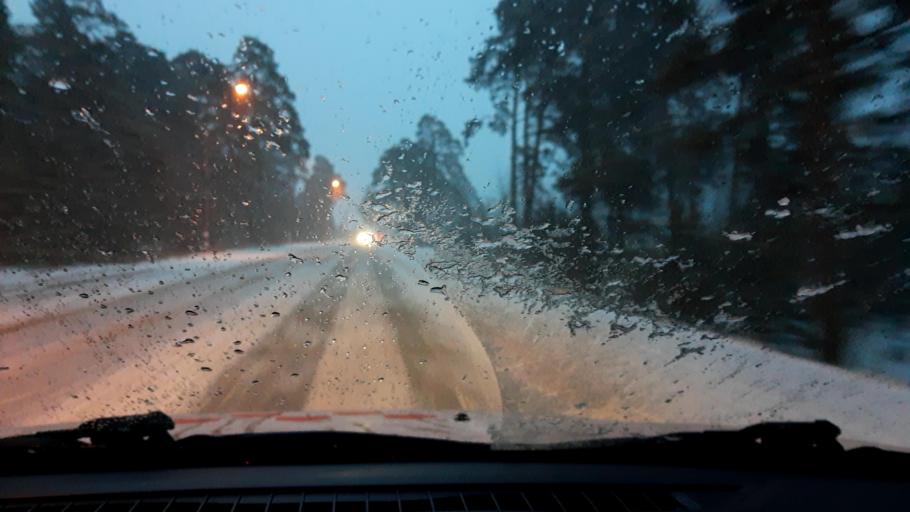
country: RU
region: Nizjnij Novgorod
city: Bor
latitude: 56.3294
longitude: 44.1231
